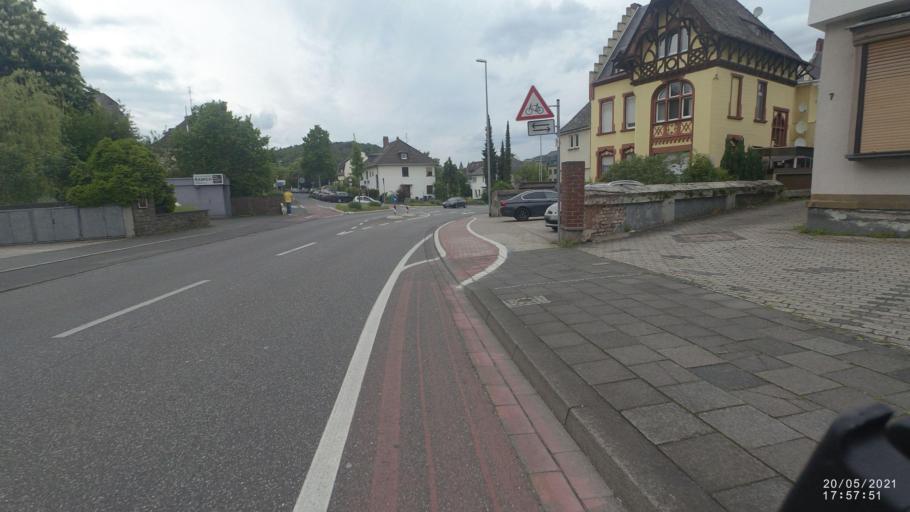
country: DE
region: Rheinland-Pfalz
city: Andernach
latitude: 50.4341
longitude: 7.4013
